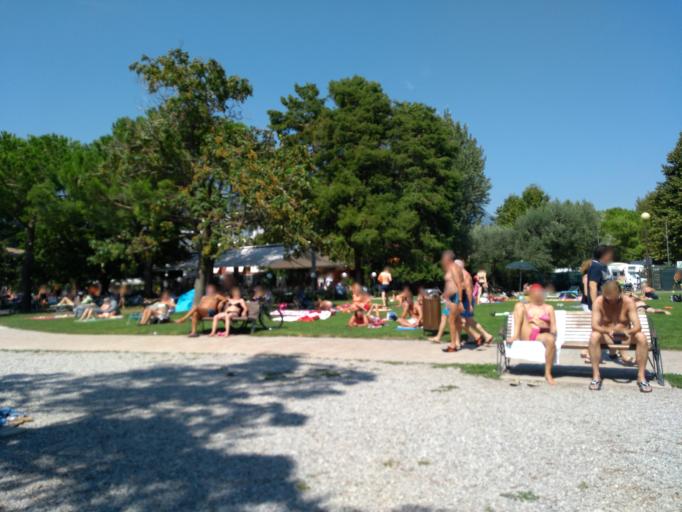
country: IT
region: Trentino-Alto Adige
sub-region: Provincia di Trento
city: Riva del Garda
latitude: 45.8789
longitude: 10.8543
